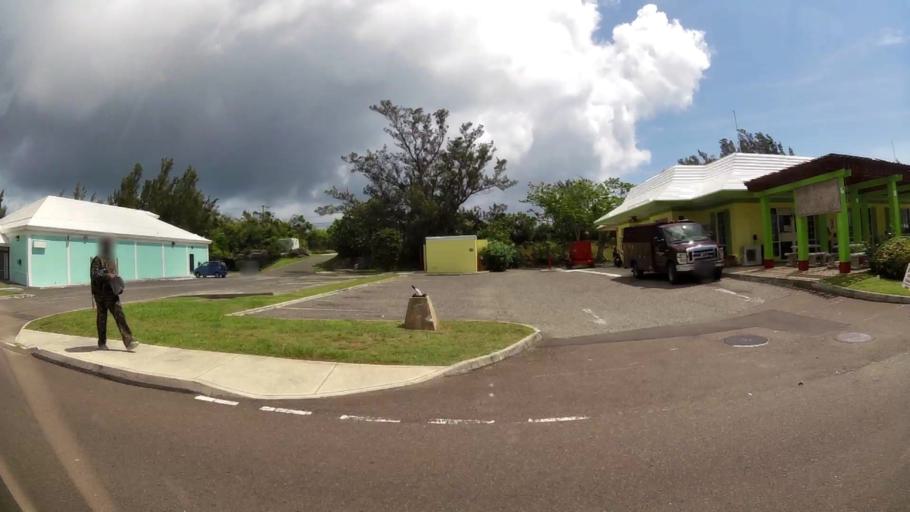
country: BM
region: Saint George
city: Saint George
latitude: 32.3652
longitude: -64.6675
